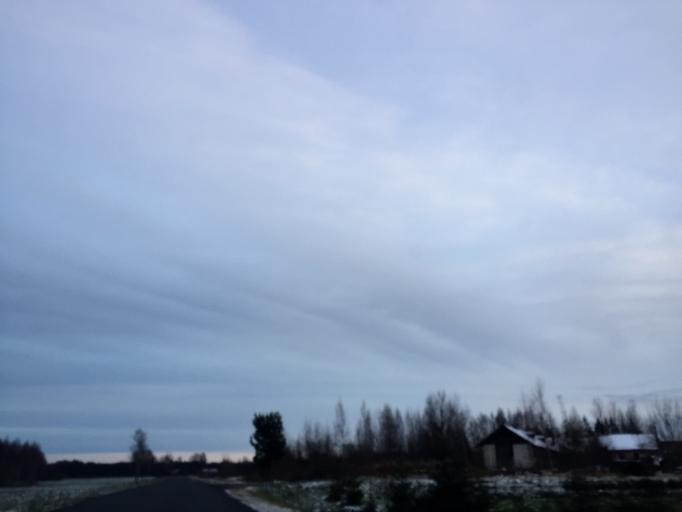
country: LV
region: Aloja
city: Aloja
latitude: 57.6485
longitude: 24.9965
